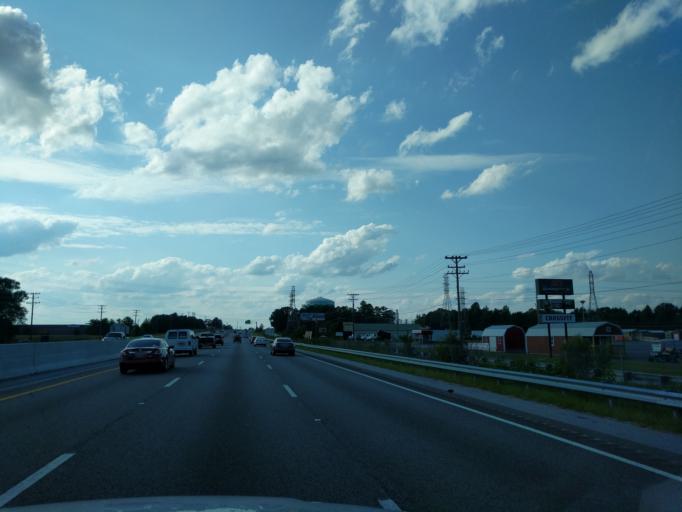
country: US
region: South Carolina
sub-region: Greenville County
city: Fountain Inn
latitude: 34.6915
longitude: -82.2234
